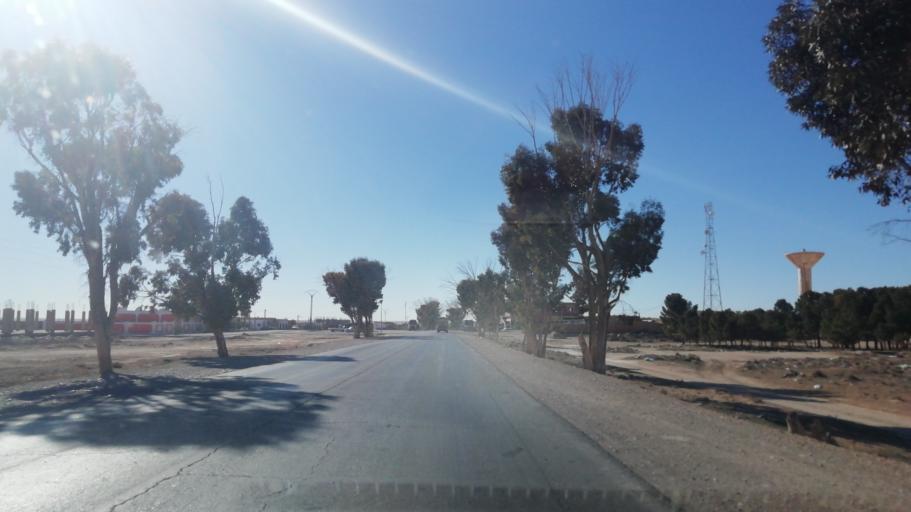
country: DZ
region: Saida
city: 'Ain el Hadjar
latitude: 34.1586
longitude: 0.0711
